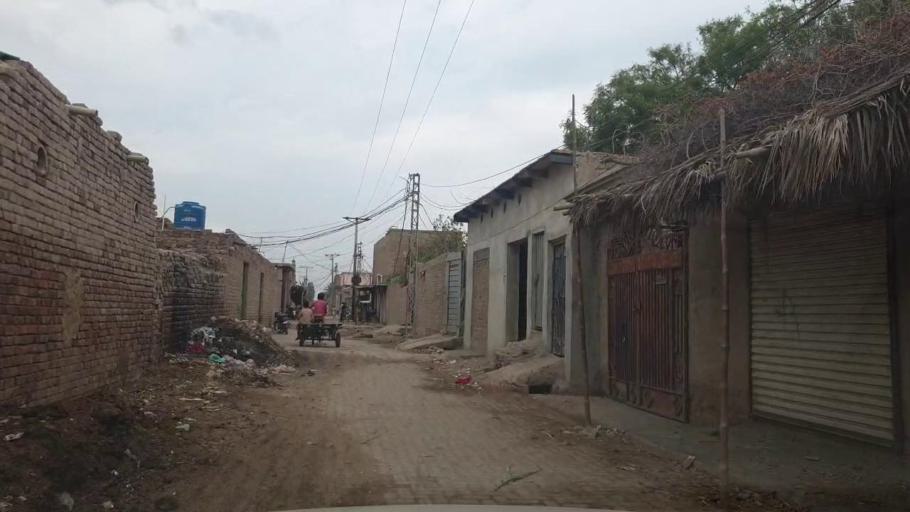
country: PK
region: Sindh
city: Khairpur
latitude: 27.5428
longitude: 68.7394
